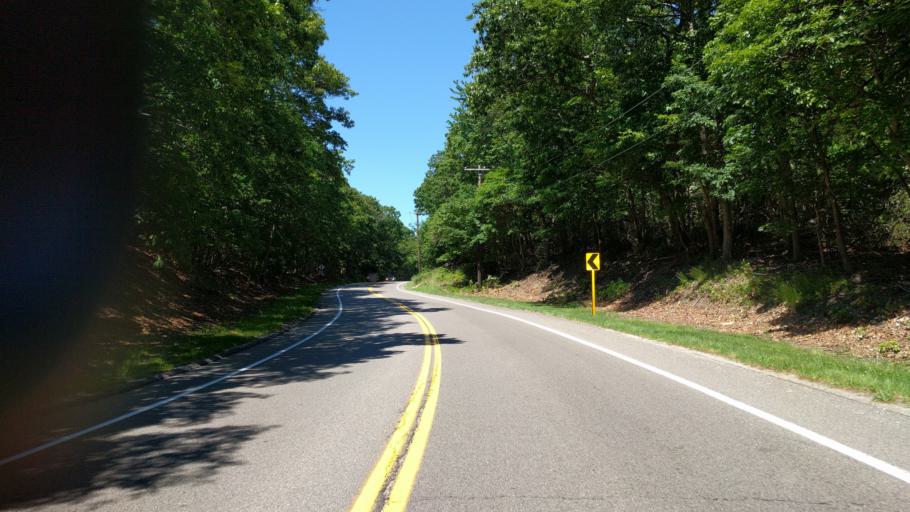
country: US
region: New York
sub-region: Suffolk County
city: Noyack
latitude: 40.9706
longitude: -72.3783
